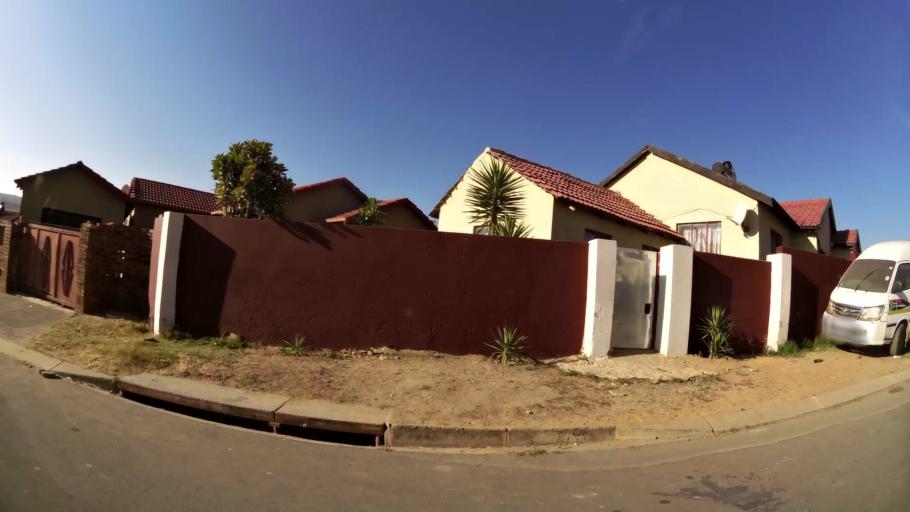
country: ZA
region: Gauteng
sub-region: City of Johannesburg Metropolitan Municipality
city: Modderfontein
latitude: -26.0424
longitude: 28.1522
